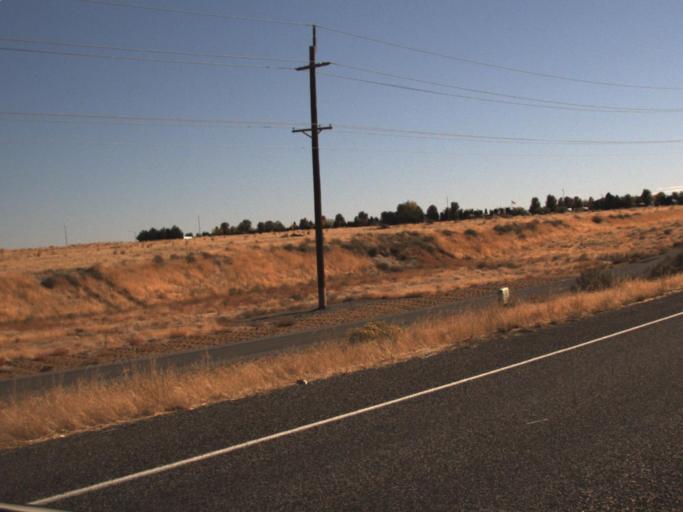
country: US
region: Washington
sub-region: Benton County
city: West Richland
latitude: 46.3280
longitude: -119.3214
